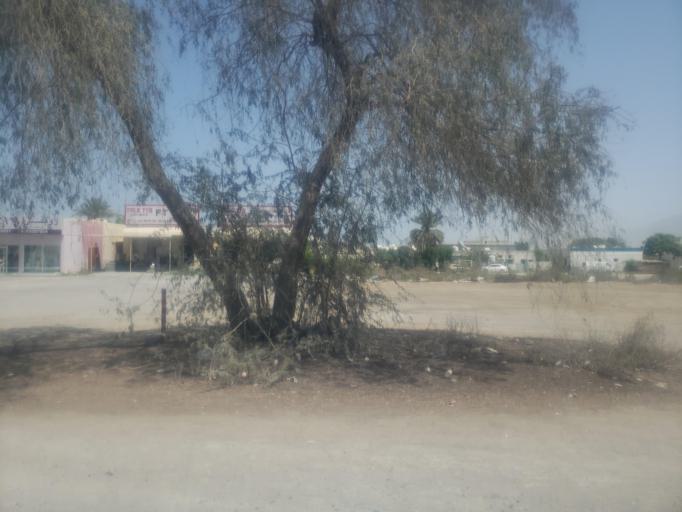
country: AE
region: Ra's al Khaymah
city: Ras al-Khaimah
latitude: 25.8045
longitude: 55.9647
